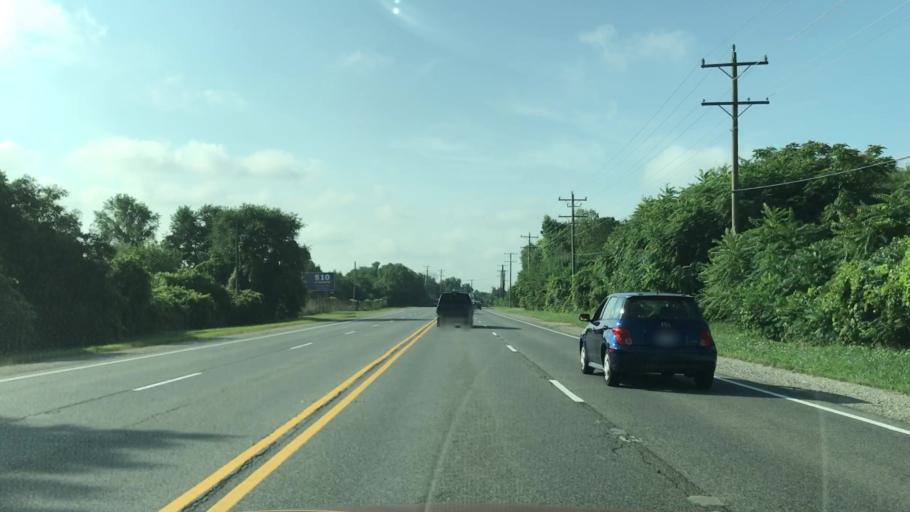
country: US
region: Illinois
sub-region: Will County
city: Lockport
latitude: 41.6148
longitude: -88.0766
